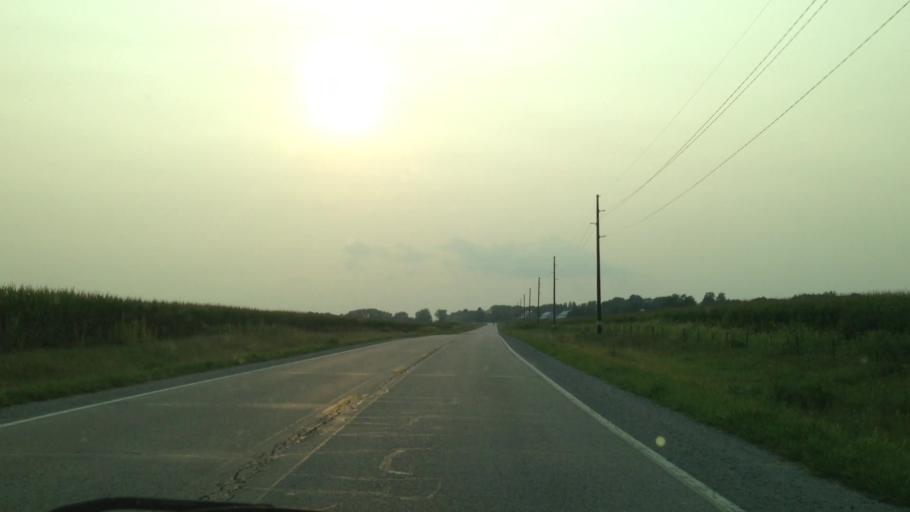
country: US
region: Iowa
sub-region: Iowa County
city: Marengo
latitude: 41.8032
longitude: -91.9496
